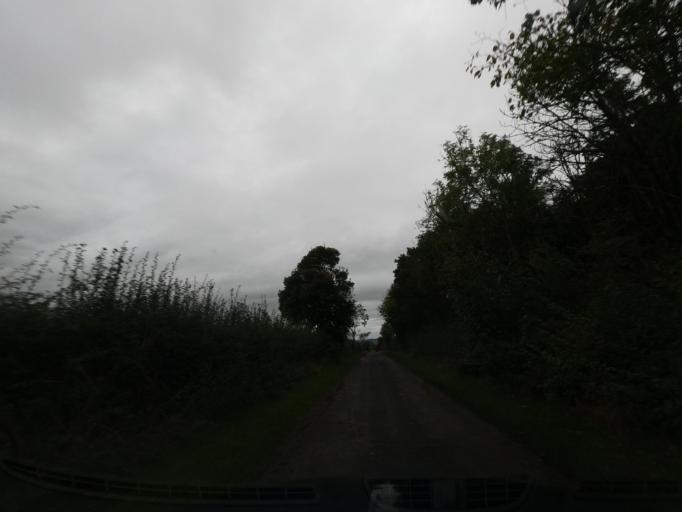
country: GB
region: England
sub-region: Northumberland
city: Ford
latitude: 55.6969
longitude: -2.0860
